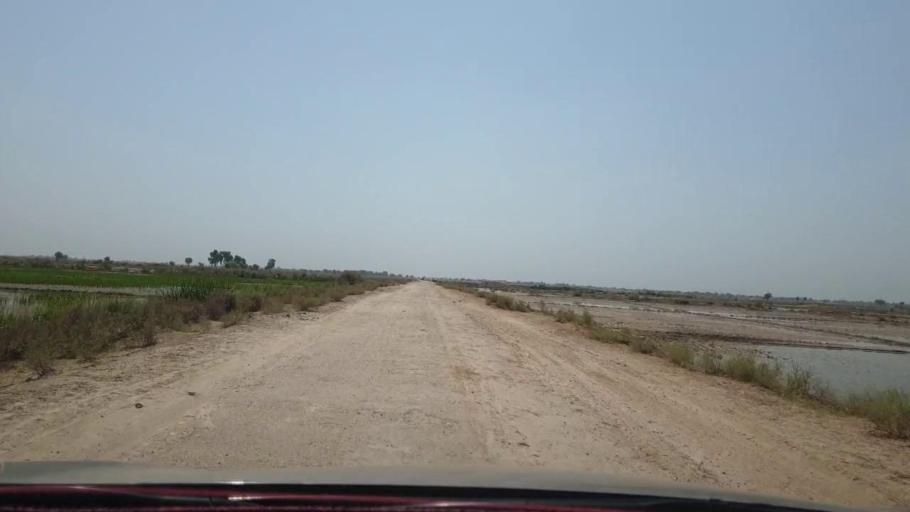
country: PK
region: Sindh
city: Kambar
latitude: 27.5846
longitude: 67.8765
